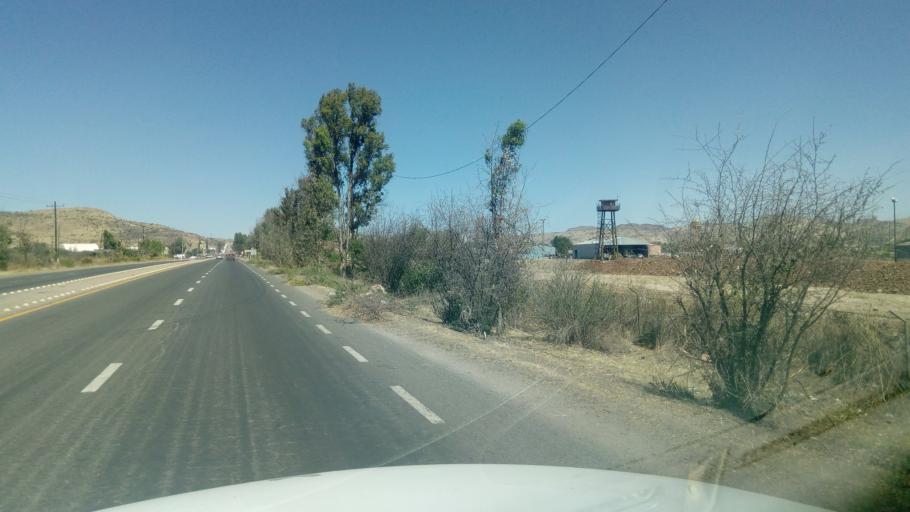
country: MX
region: Durango
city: Victoria de Durango
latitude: 24.0726
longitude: -104.6585
